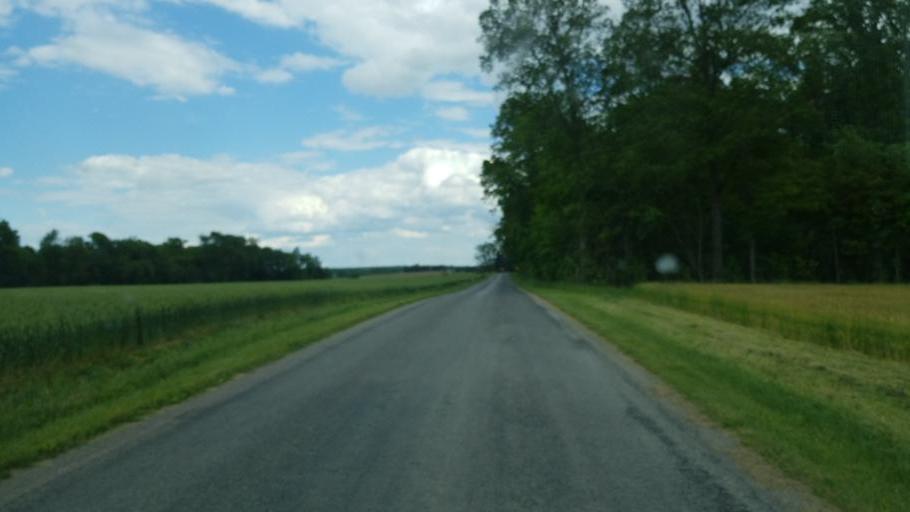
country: US
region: Ohio
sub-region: Richland County
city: Shelby
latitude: 40.9384
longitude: -82.6181
